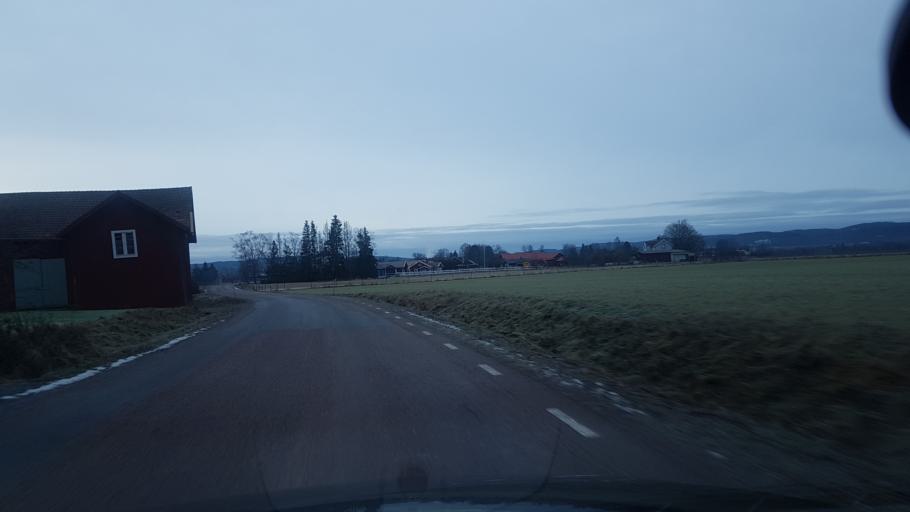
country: SE
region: Dalarna
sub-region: Saters Kommun
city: Saeter
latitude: 60.4279
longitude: 15.6567
